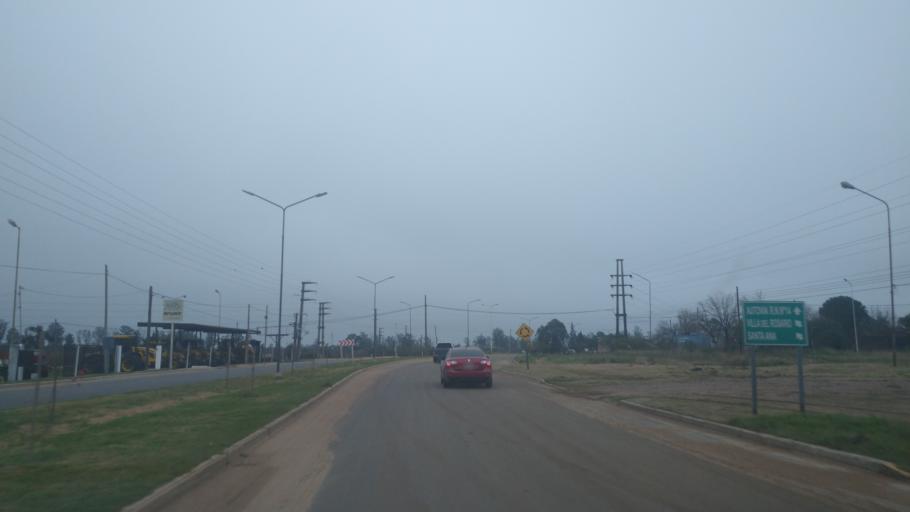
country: AR
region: Entre Rios
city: Chajari
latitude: -30.7623
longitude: -58.0133
